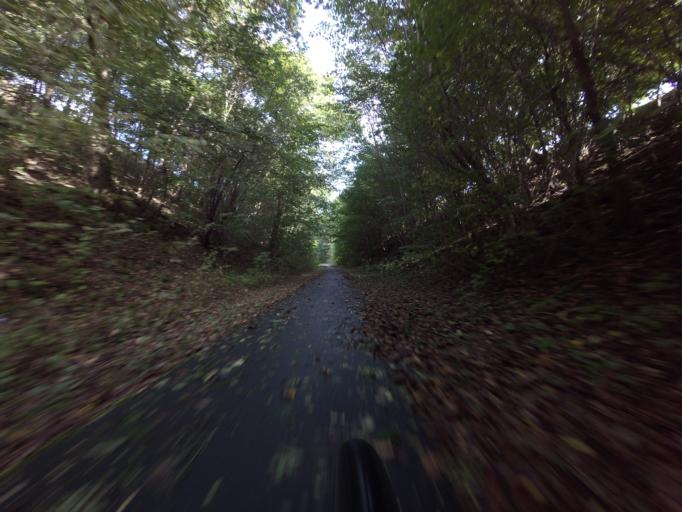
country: DK
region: Central Jutland
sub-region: Viborg Kommune
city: Bjerringbro
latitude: 56.4618
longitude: 9.5885
